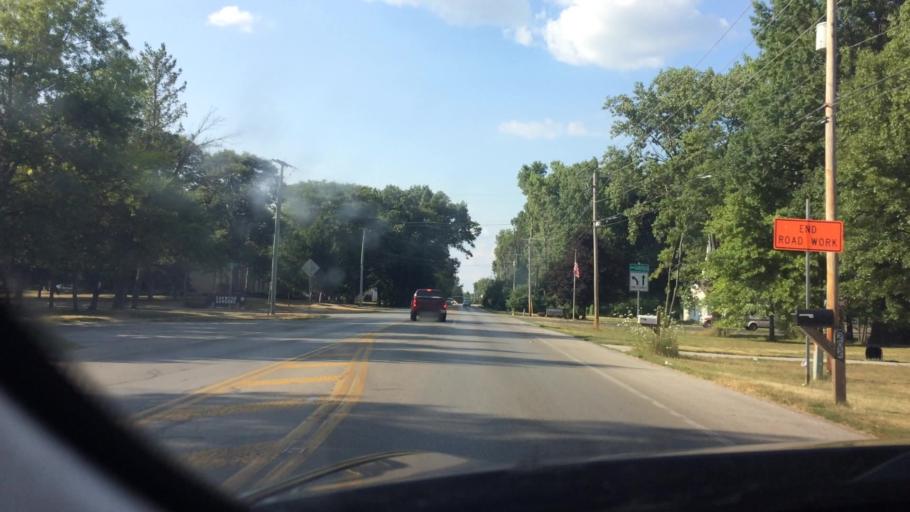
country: US
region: Ohio
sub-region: Lucas County
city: Holland
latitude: 41.6414
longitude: -83.7036
